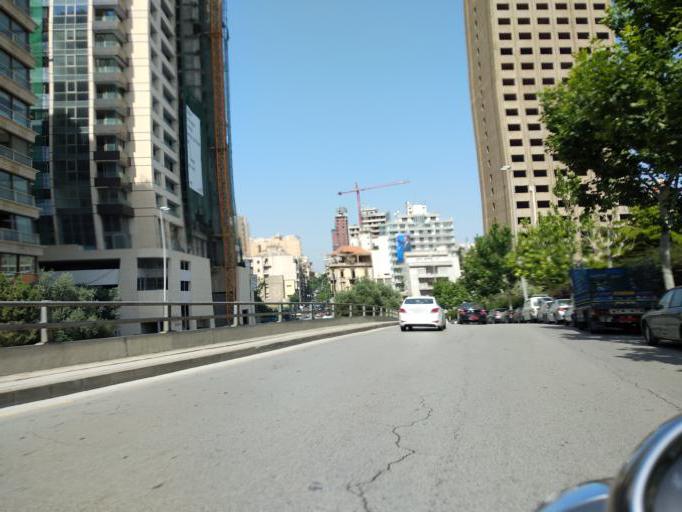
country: LB
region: Beyrouth
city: Beirut
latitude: 33.8949
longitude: 35.4977
